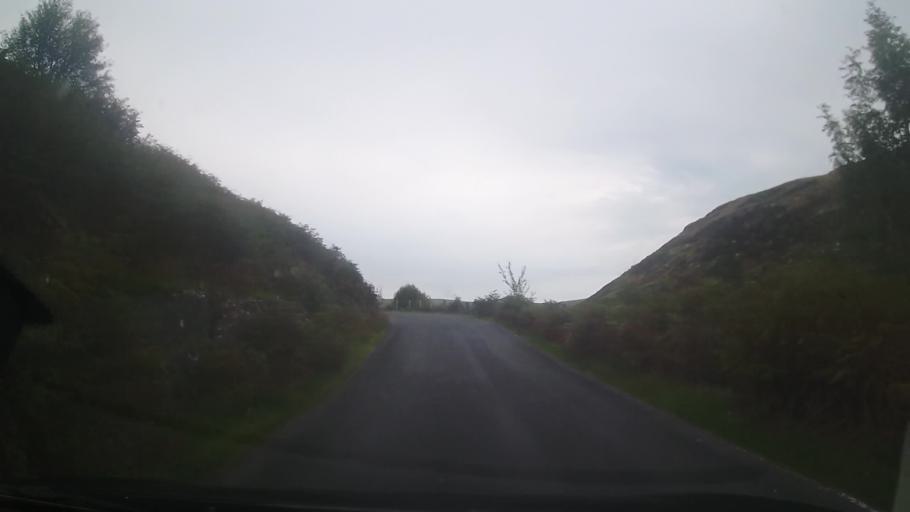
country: GB
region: Wales
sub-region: Sir Powys
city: Rhayader
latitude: 52.3023
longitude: -3.6239
